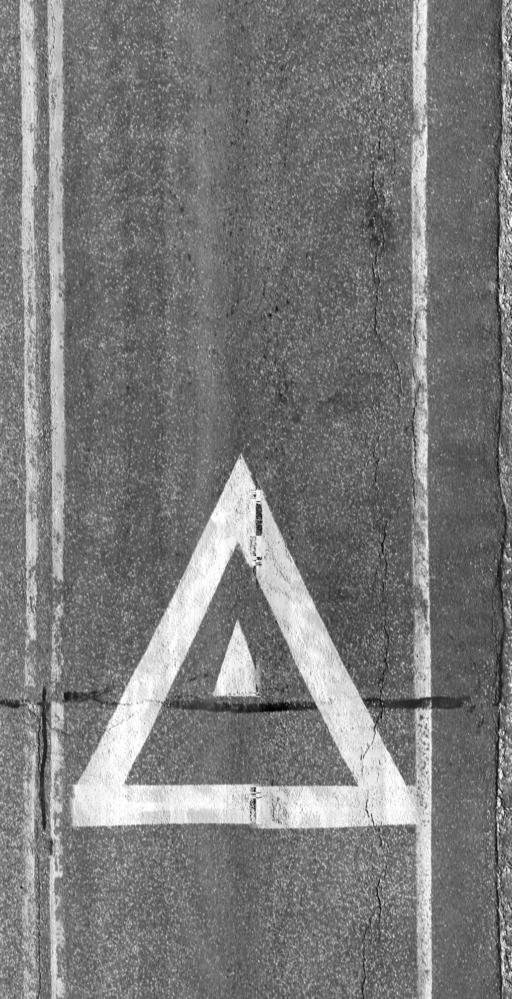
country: US
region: Vermont
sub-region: Chittenden County
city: Jericho
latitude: 44.4955
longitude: -73.0023
